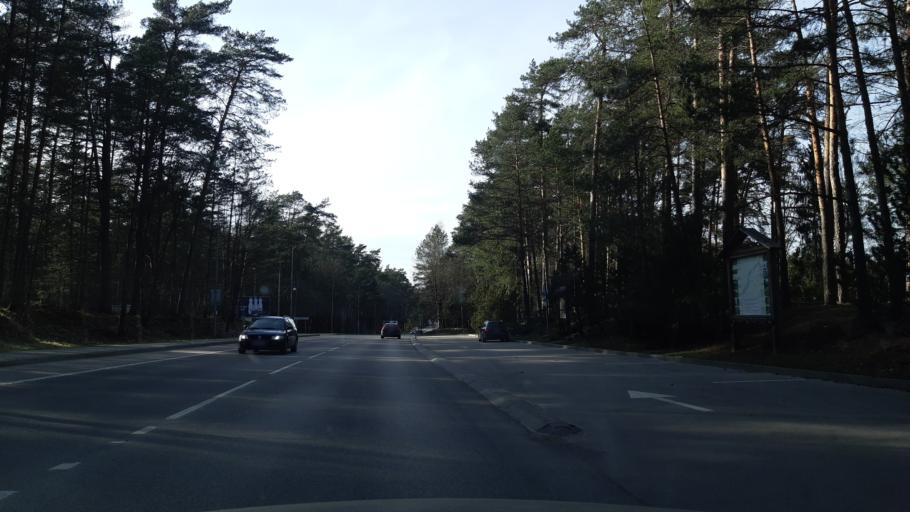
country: LT
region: Alytaus apskritis
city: Druskininkai
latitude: 54.0063
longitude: 24.0040
